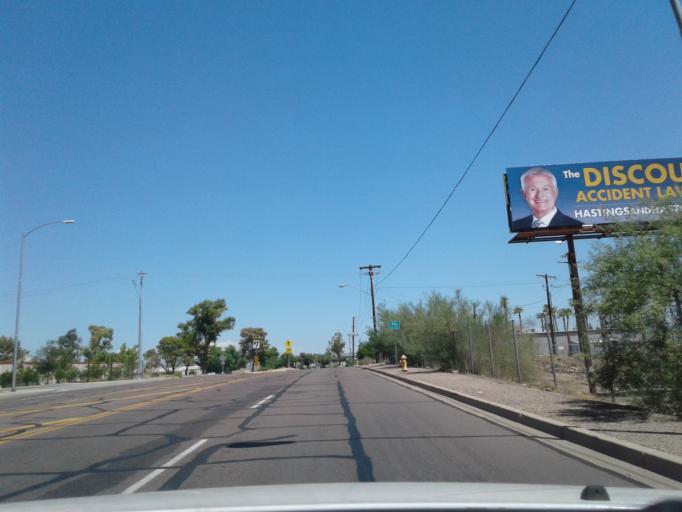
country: US
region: Arizona
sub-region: Maricopa County
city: Phoenix
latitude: 33.4206
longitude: -112.0302
